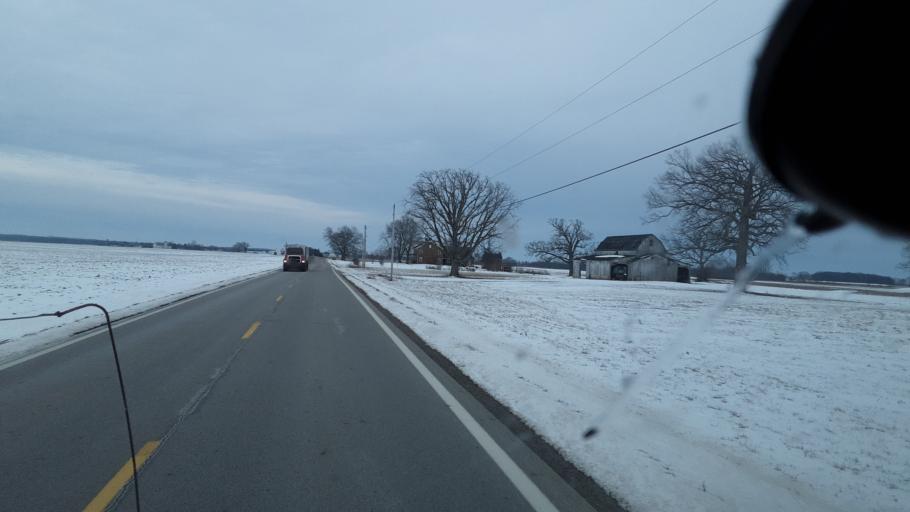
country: US
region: Ohio
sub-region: Pickaway County
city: Circleville
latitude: 39.6185
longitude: -83.0175
